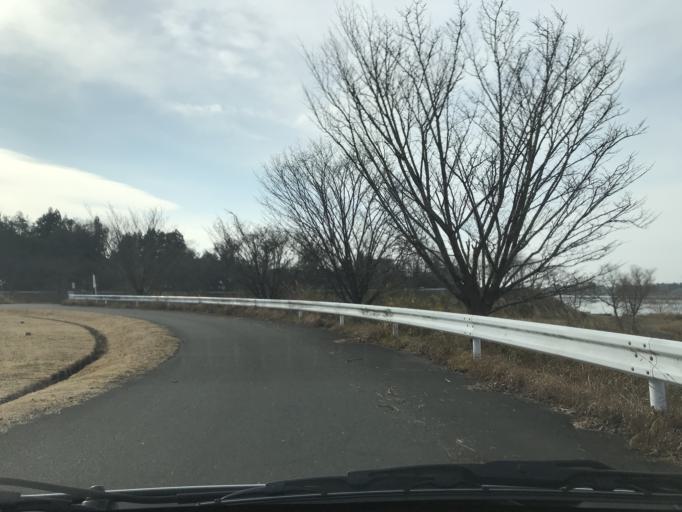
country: JP
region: Miyagi
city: Wakuya
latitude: 38.6992
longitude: 141.1457
